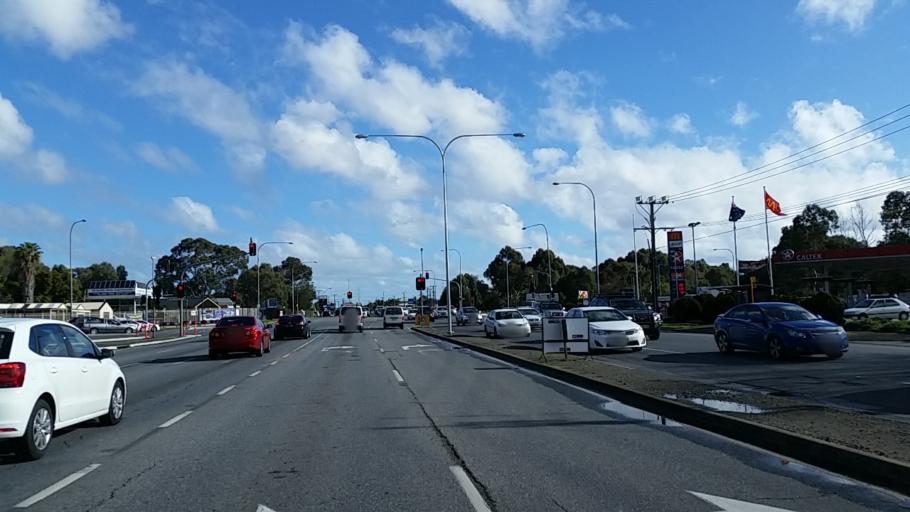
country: AU
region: South Australia
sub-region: Salisbury
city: Ingle Farm
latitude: -34.8238
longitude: 138.6183
